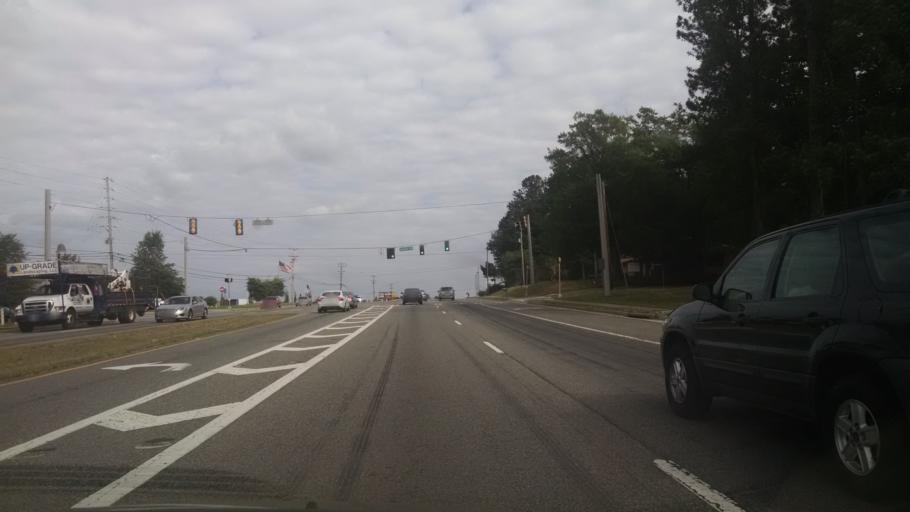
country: US
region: Georgia
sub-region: Forsyth County
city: Cumming
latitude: 34.1776
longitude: -84.1309
